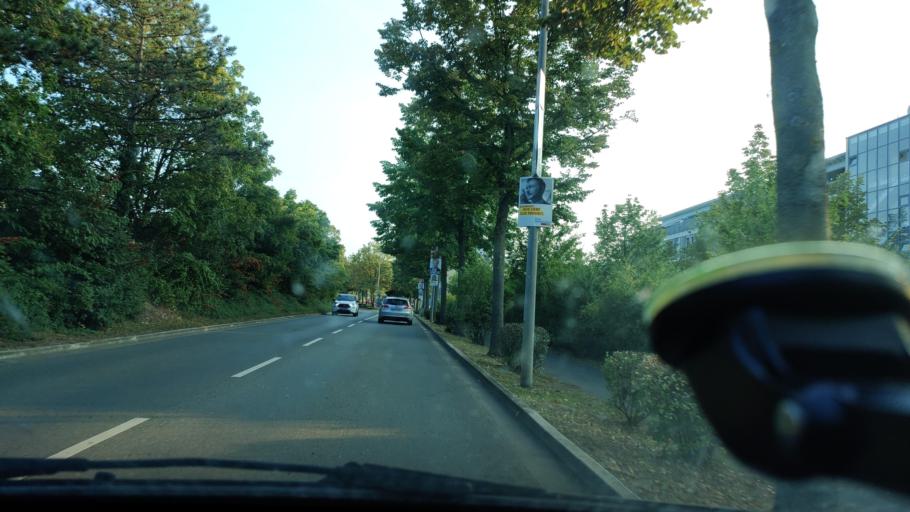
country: DE
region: North Rhine-Westphalia
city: Sankt Augustin
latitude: 50.7819
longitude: 7.1855
